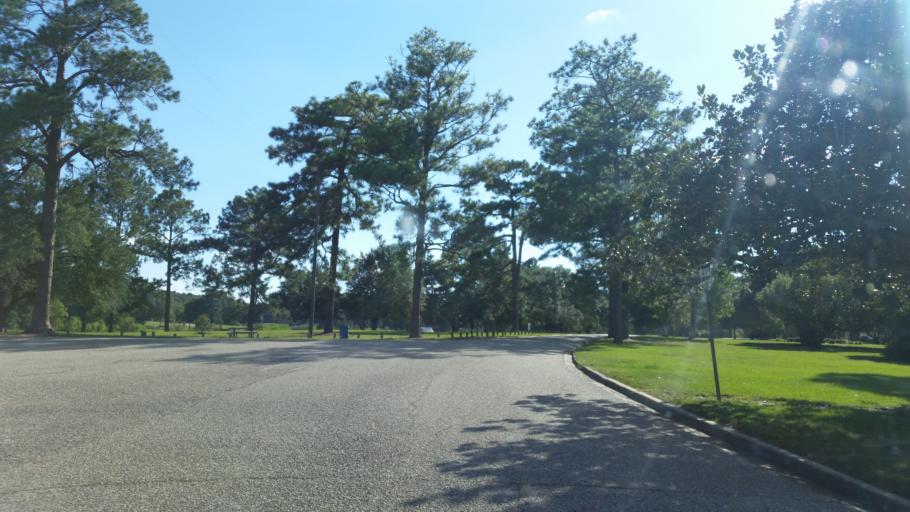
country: US
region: Alabama
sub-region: Mobile County
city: Prichard
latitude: 30.7071
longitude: -88.1594
